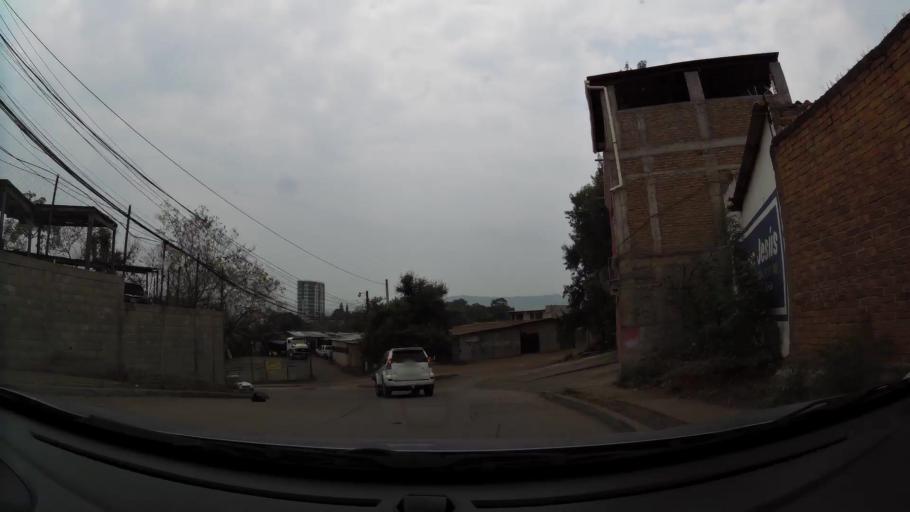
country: HN
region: Francisco Morazan
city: Tegucigalpa
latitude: 14.0730
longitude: -87.1770
